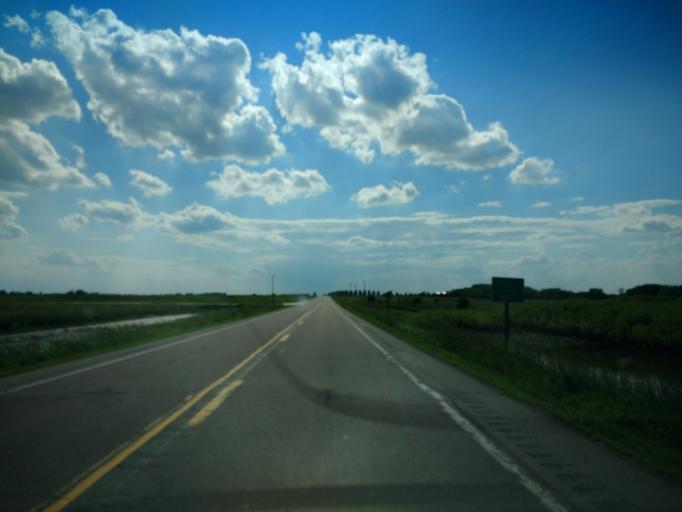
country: US
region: Iowa
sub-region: Clay County
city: Spencer
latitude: 43.1842
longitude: -95.1935
